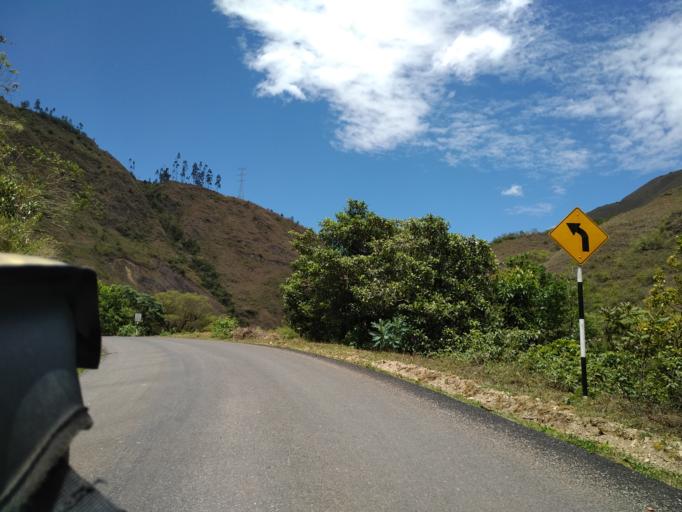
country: PE
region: Amazonas
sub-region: Provincia de Chachapoyas
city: Montevideo
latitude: -6.6605
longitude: -77.7993
